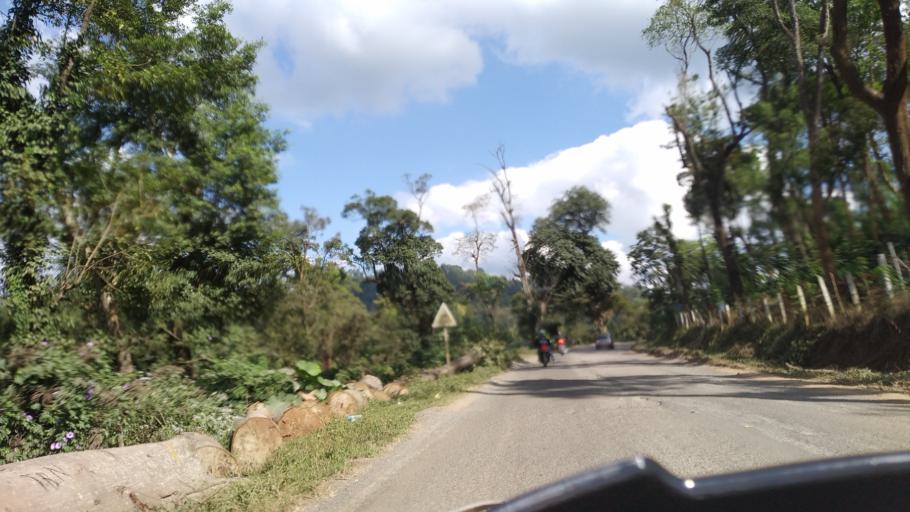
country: IN
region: Karnataka
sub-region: Kodagu
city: Ponnampet
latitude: 11.9633
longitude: 76.0573
